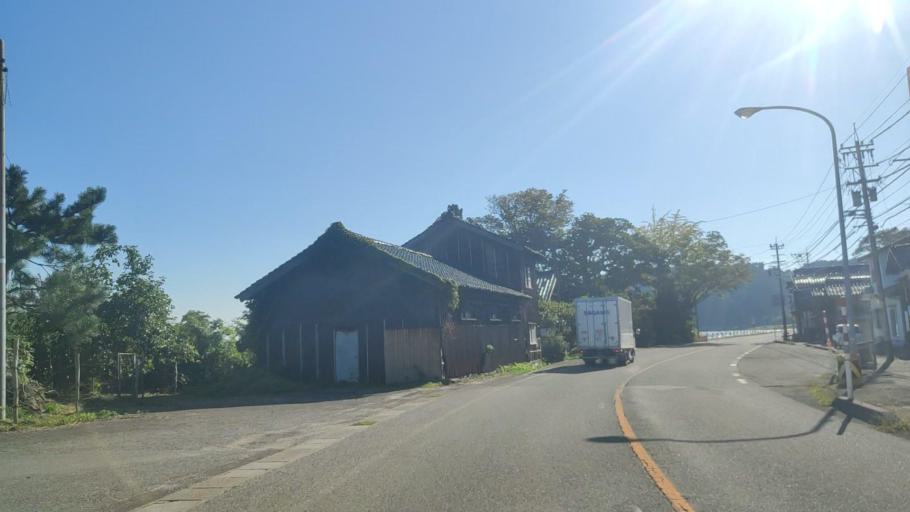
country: JP
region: Ishikawa
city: Nanao
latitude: 37.1929
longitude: 136.9104
